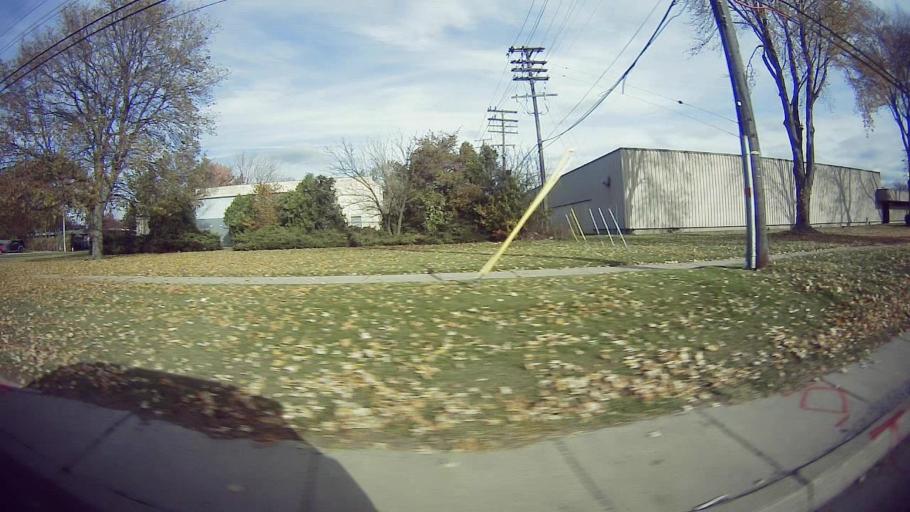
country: US
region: Michigan
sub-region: Macomb County
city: Warren
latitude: 42.4626
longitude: -83.0484
